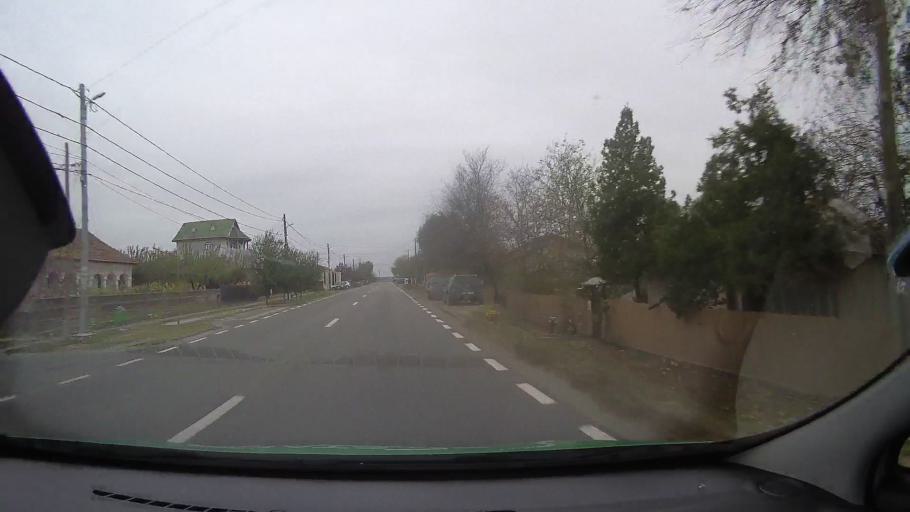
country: RO
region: Ialomita
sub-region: Comuna Slobozia
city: Slobozia
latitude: 44.5981
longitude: 27.3896
